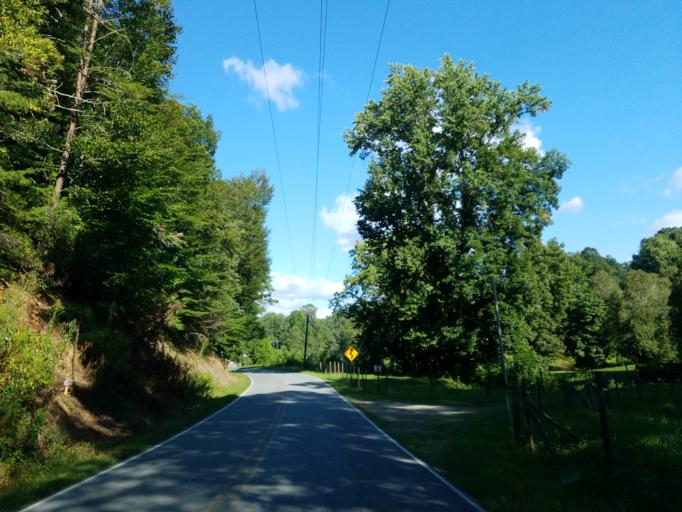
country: US
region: Georgia
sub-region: Fannin County
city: Blue Ridge
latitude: 34.7600
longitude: -84.2170
